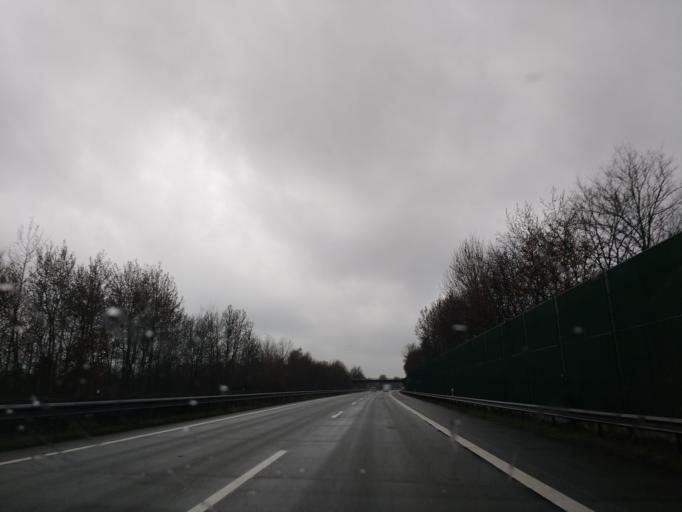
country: DE
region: Lower Saxony
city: Langen
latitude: 53.5985
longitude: 8.6483
